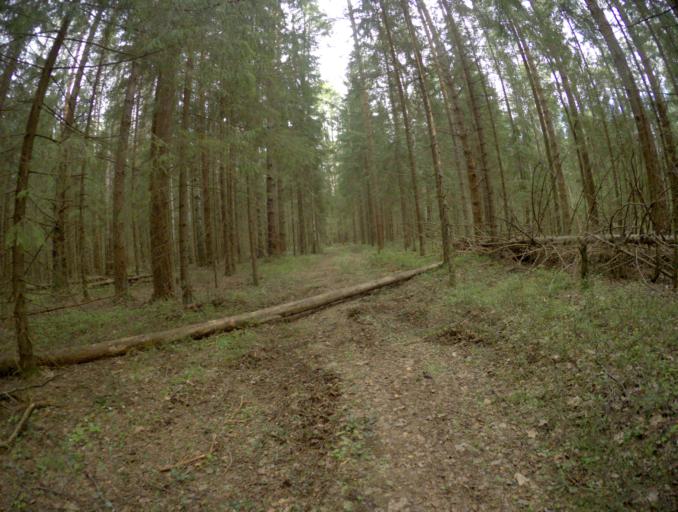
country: RU
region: Vladimir
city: Golovino
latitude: 55.8998
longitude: 40.4701
